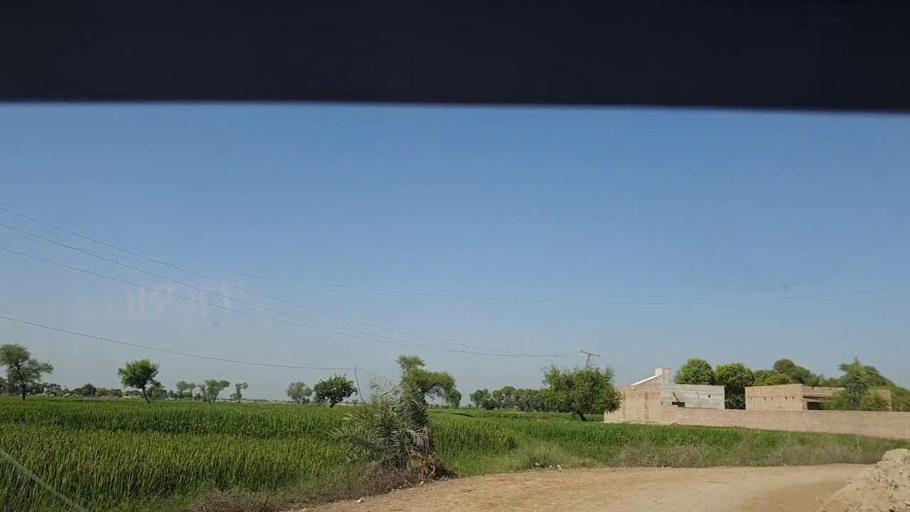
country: PK
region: Sindh
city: Ghauspur
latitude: 28.2038
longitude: 69.0455
